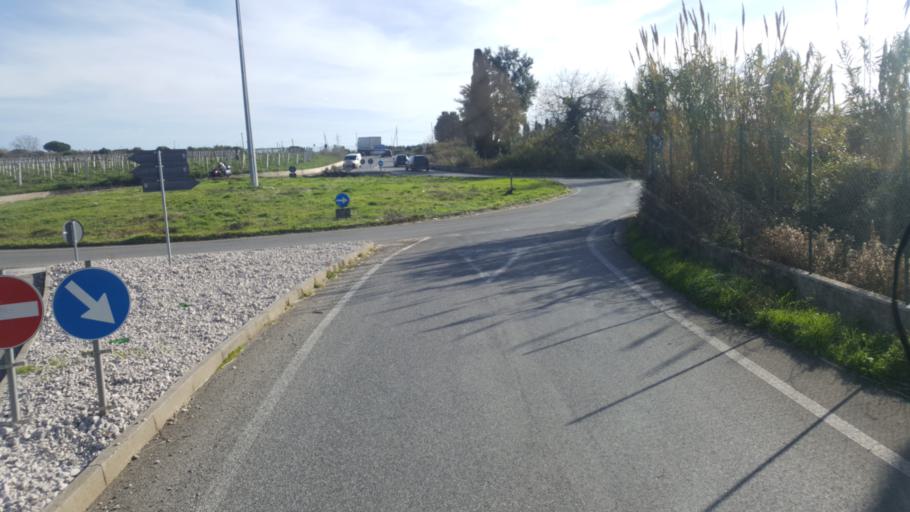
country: IT
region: Latium
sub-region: Citta metropolitana di Roma Capitale
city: Mantiglia di Ardea
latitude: 41.6703
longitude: 12.6366
